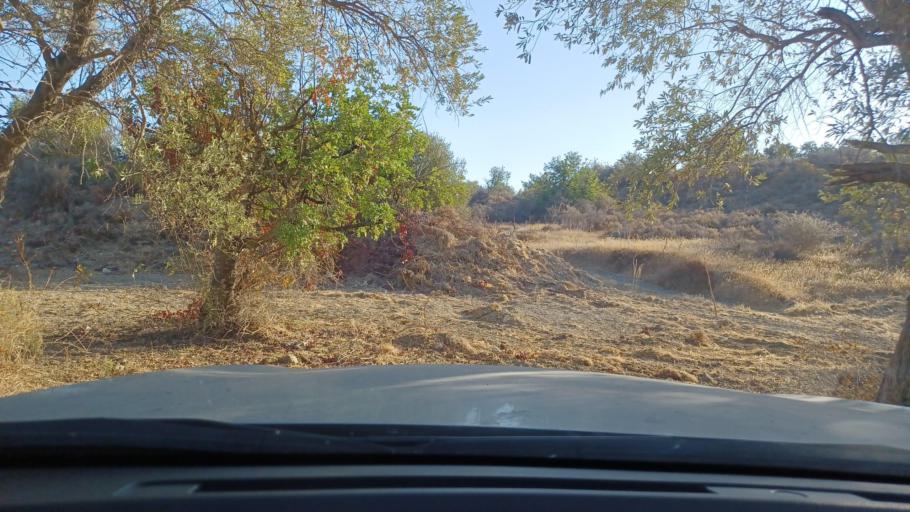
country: CY
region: Pafos
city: Polis
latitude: 35.0042
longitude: 32.5039
